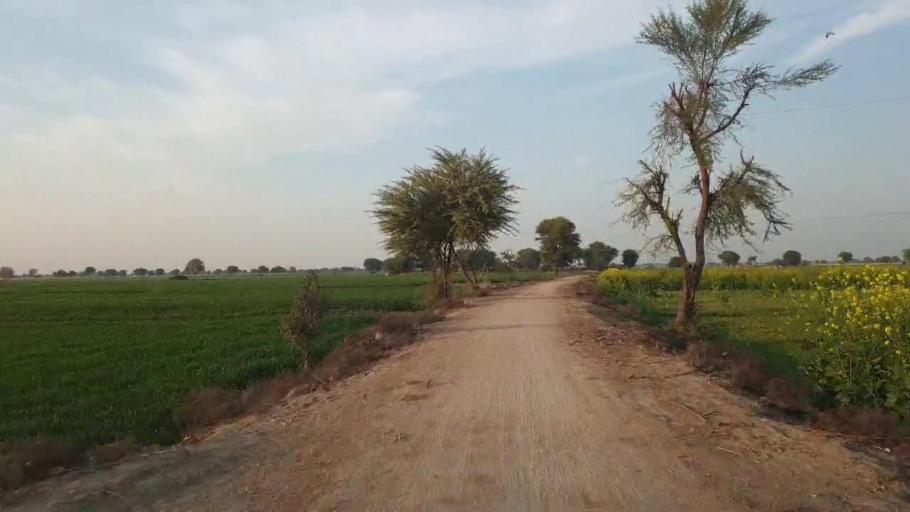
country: PK
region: Sindh
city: Shahpur Chakar
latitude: 26.1735
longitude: 68.6225
